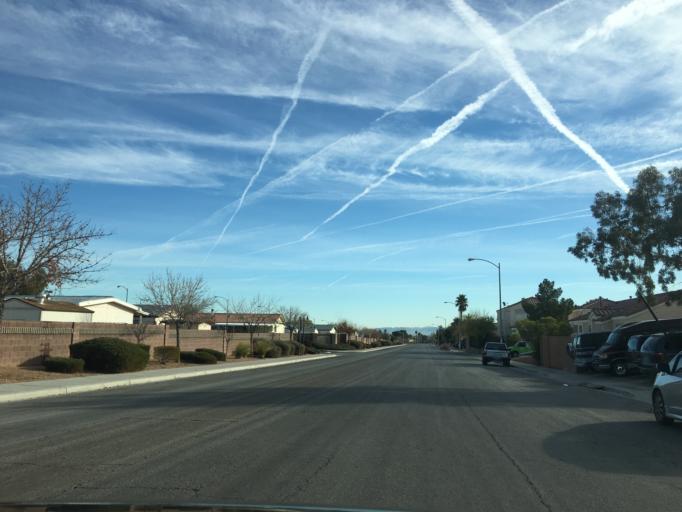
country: US
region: Nevada
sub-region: Clark County
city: Enterprise
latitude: 36.0173
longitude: -115.1778
